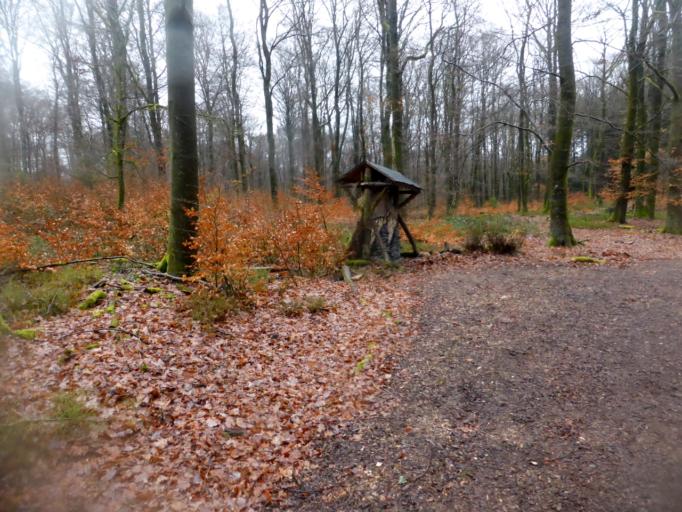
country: LU
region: Diekirch
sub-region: Canton de Redange
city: Ell
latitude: 49.7819
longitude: 5.8257
